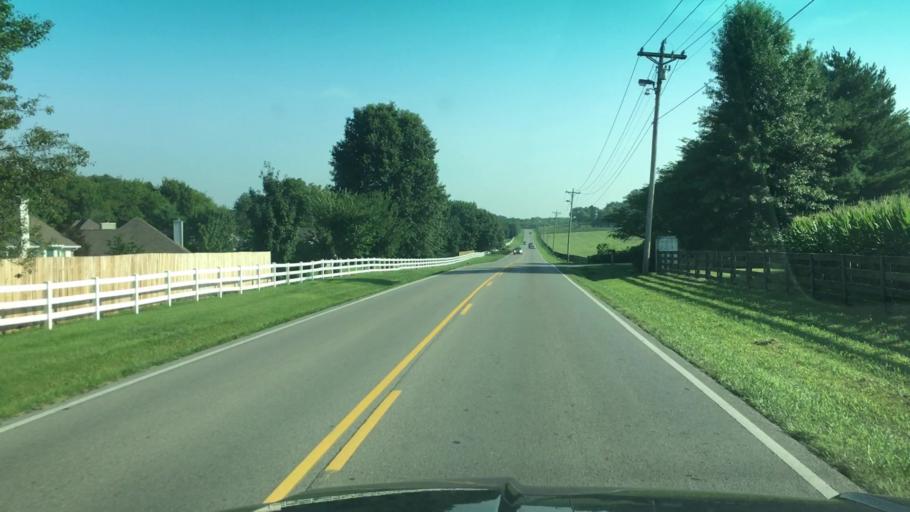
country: US
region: Tennessee
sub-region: Williamson County
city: Thompson's Station
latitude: 35.7822
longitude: -86.8789
